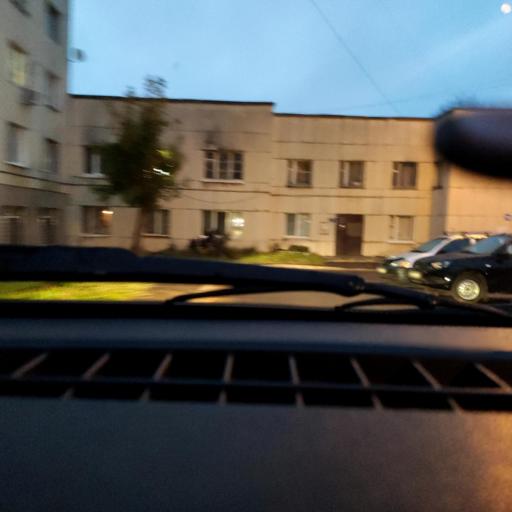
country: RU
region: Bashkortostan
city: Ufa
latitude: 54.8186
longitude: 56.1259
